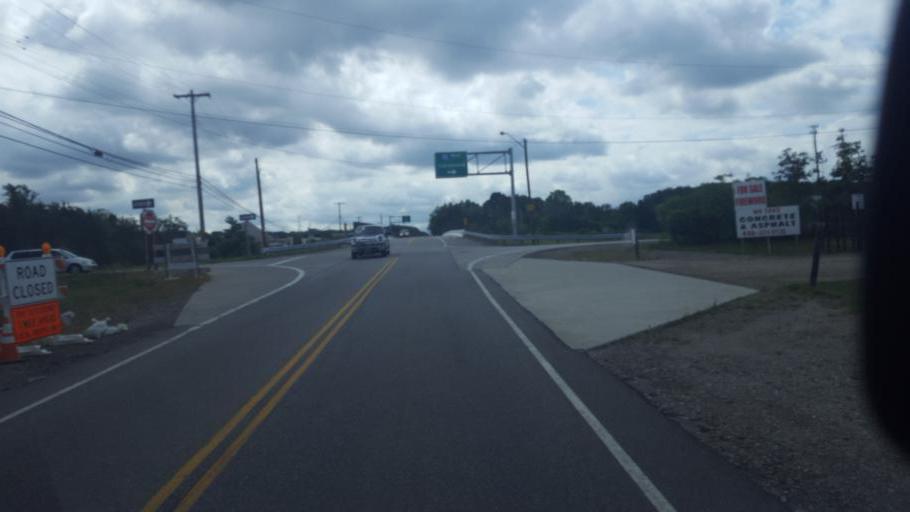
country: US
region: Ohio
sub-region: Lake County
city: Perry
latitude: 41.7096
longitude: -81.1764
